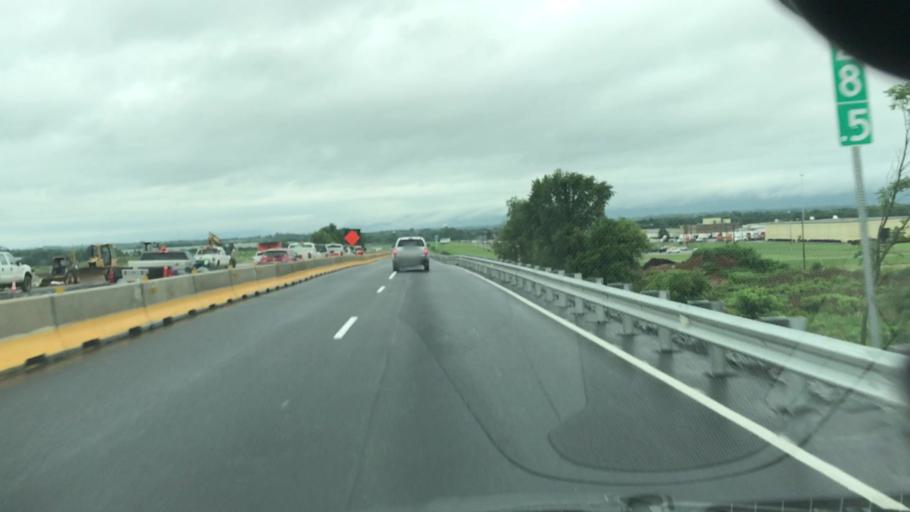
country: US
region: Pennsylvania
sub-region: Cumberland County
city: Schlusser
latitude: 40.2246
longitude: -77.1148
